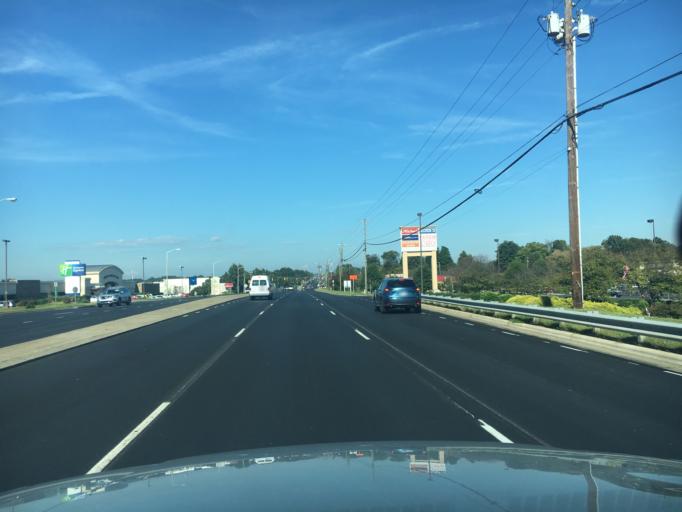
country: US
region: North Carolina
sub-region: Catawba County
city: Hickory
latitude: 35.7030
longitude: -81.2956
